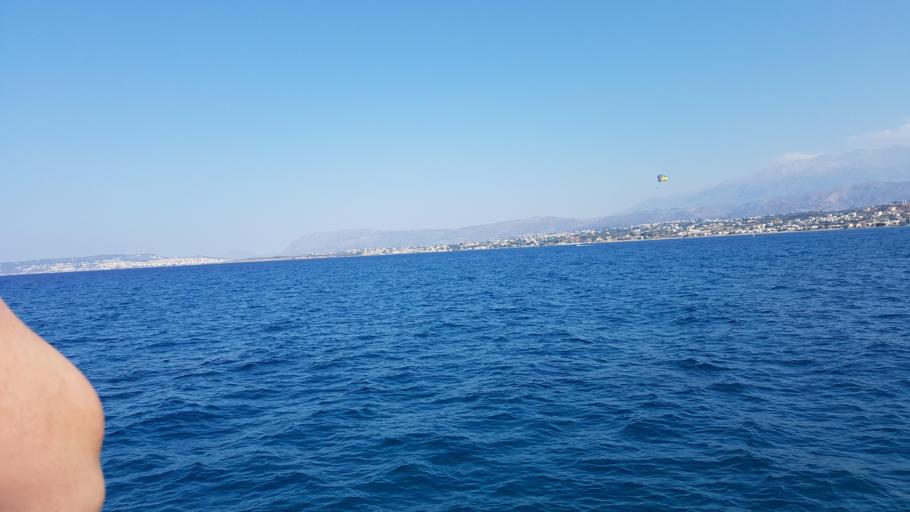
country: GR
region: Crete
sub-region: Nomos Chanias
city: Agia Marina
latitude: 35.5318
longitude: 23.9348
